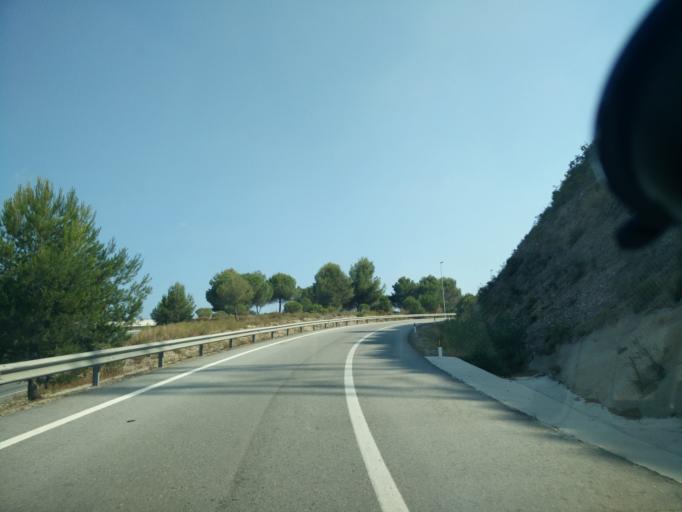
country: ES
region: Catalonia
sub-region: Provincia de Barcelona
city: Rubi
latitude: 41.5275
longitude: 2.0238
